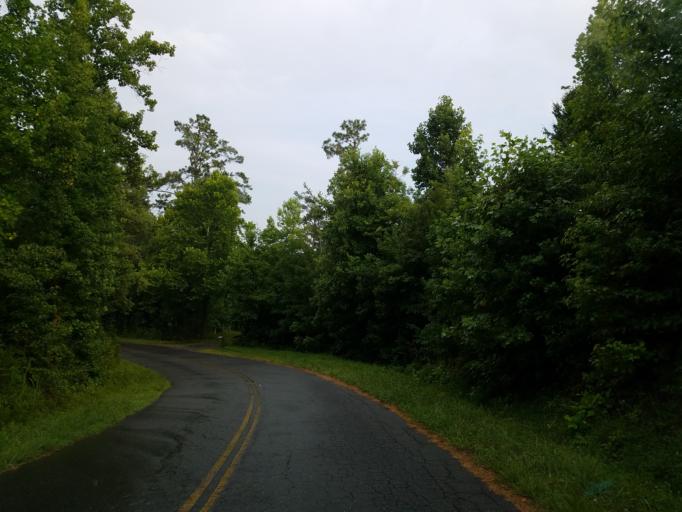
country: US
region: Georgia
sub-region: Bartow County
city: Rydal
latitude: 34.3918
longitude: -84.6614
